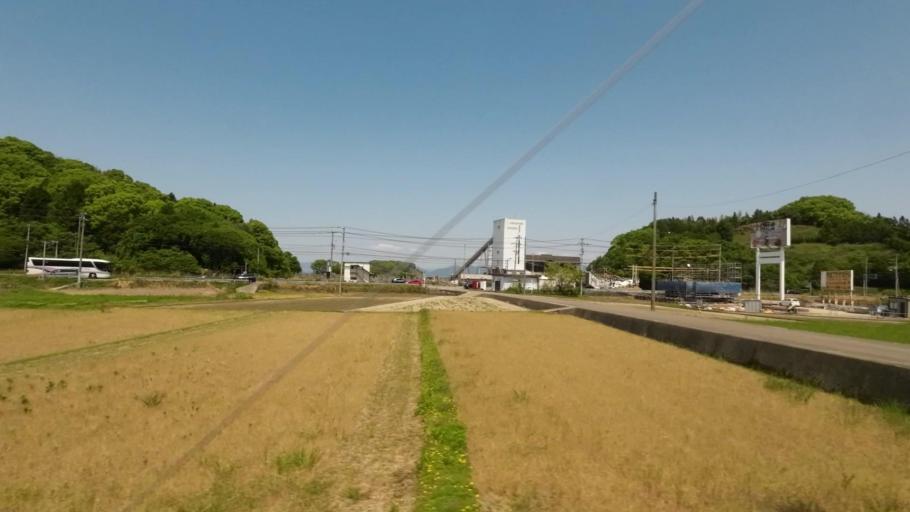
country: JP
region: Ehime
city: Hojo
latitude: 34.0598
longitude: 132.8940
